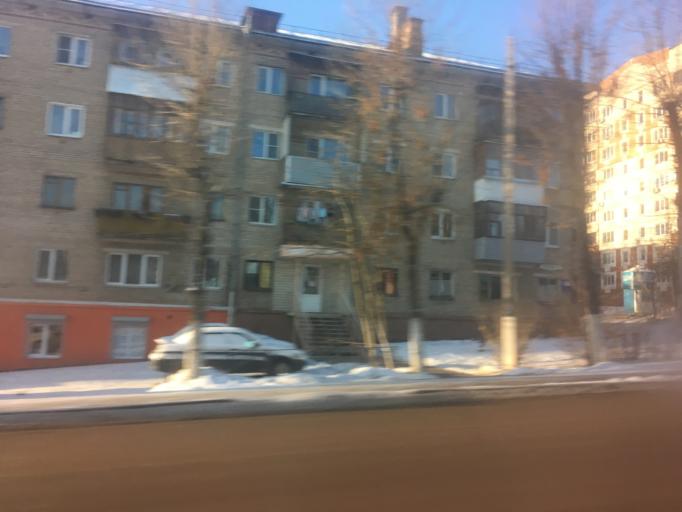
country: RU
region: Tula
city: Tula
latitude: 54.2049
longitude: 37.6771
